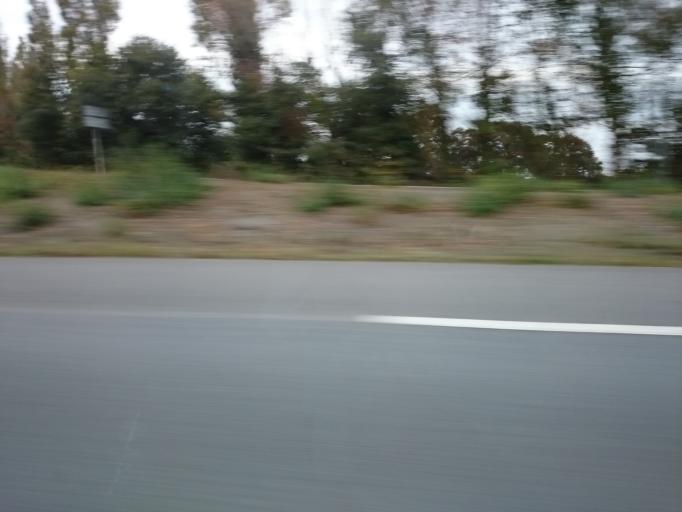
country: FR
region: Brittany
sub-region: Departement du Morbihan
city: Auray
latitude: 47.6820
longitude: -3.0220
